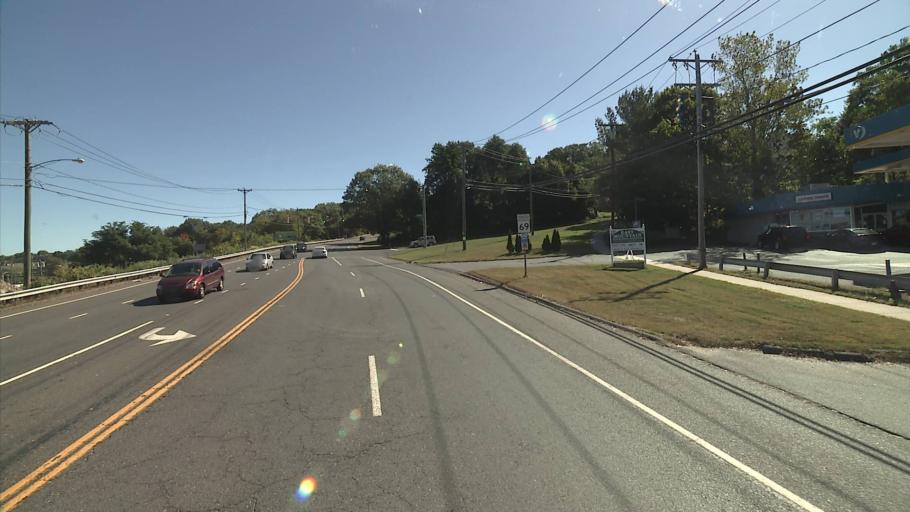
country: US
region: Connecticut
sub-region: New Haven County
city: Waterbury
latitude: 41.5368
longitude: -73.0168
